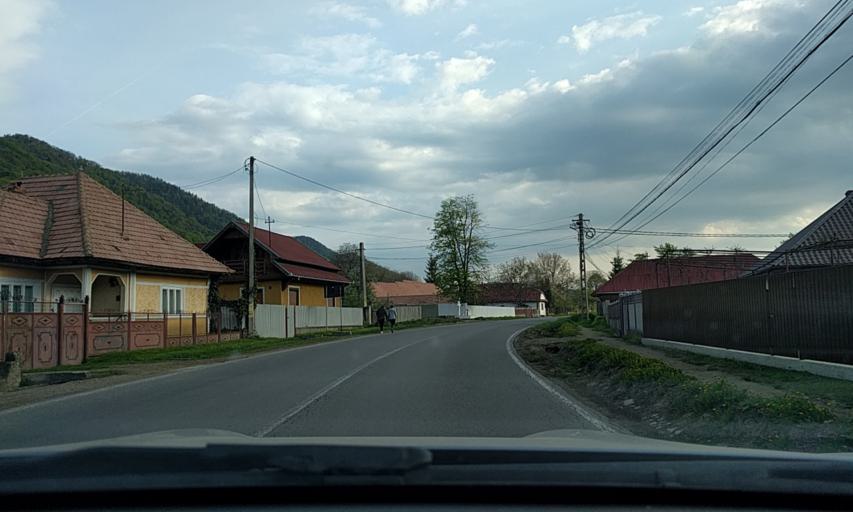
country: RO
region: Bacau
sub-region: Oras Slanic-Moldova
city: Slanic-Moldova
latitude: 46.1461
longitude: 26.4576
